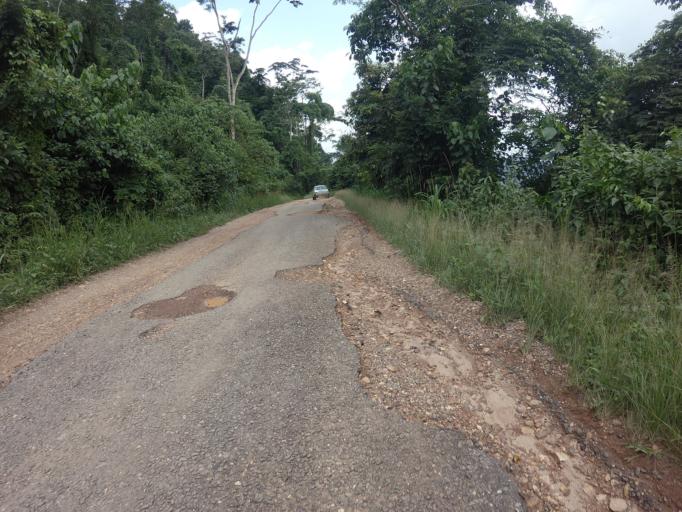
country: GH
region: Volta
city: Kpandu
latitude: 6.8424
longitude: 0.4313
